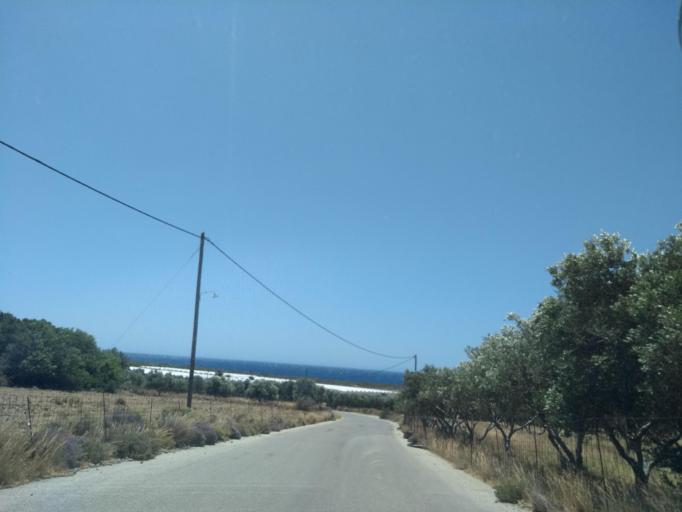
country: GR
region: Crete
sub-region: Nomos Chanias
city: Vryses
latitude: 35.3400
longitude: 23.5431
